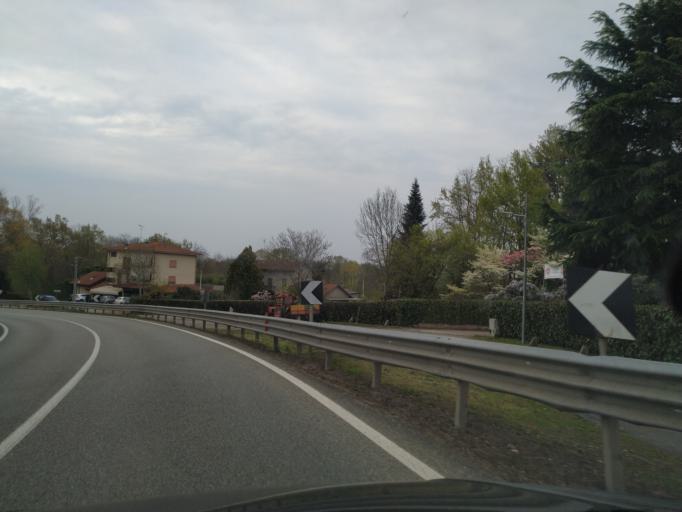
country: IT
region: Piedmont
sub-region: Provincia di Novara
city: Cureggio
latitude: 45.6680
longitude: 8.4512
